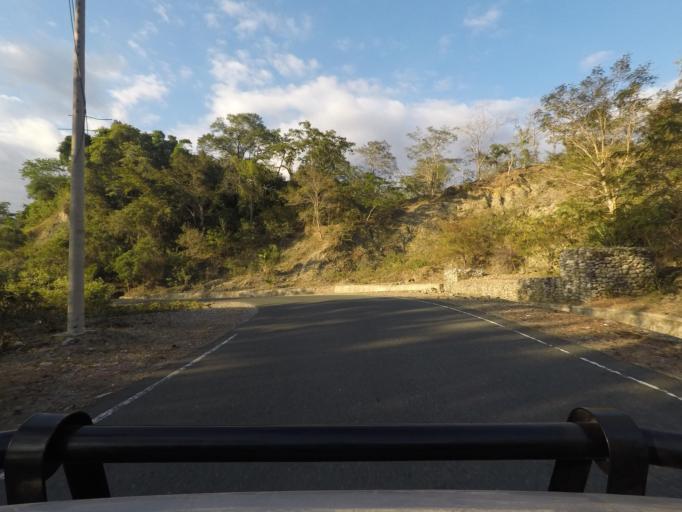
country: TL
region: Bobonaro
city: Maliana
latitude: -8.9526
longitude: 125.0921
